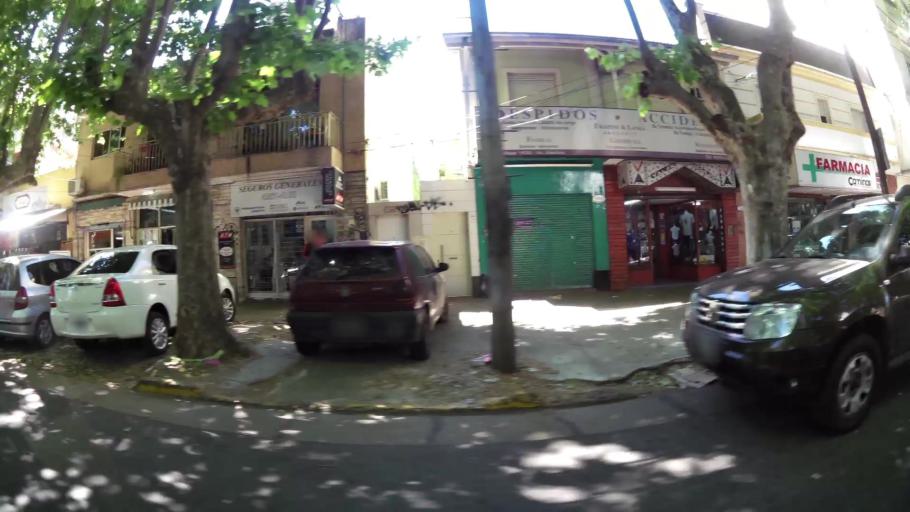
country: AR
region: Buenos Aires
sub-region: Partido de General San Martin
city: General San Martin
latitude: -34.5218
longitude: -58.5452
